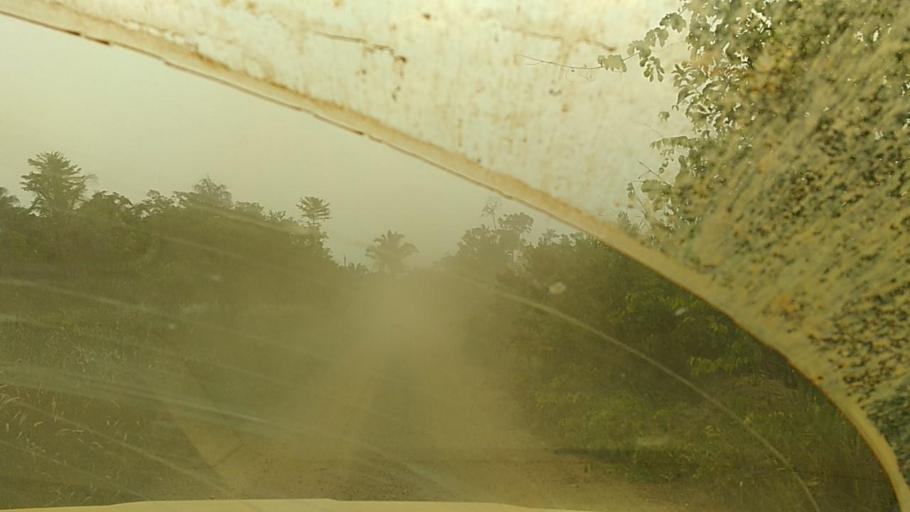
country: BR
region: Rondonia
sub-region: Porto Velho
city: Porto Velho
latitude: -8.7730
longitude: -63.1923
